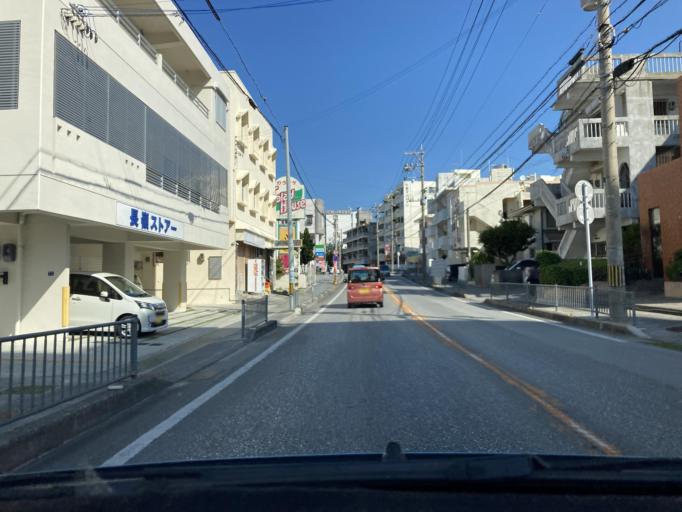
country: JP
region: Okinawa
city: Tomigusuku
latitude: 26.1885
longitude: 127.6602
